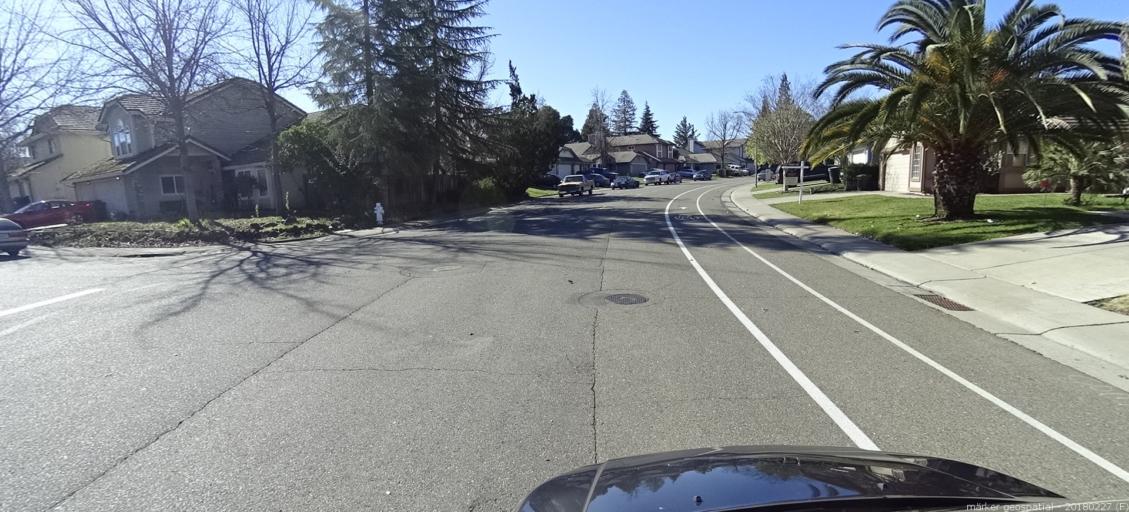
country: US
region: California
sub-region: Sacramento County
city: Antelope
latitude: 38.7174
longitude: -121.3514
